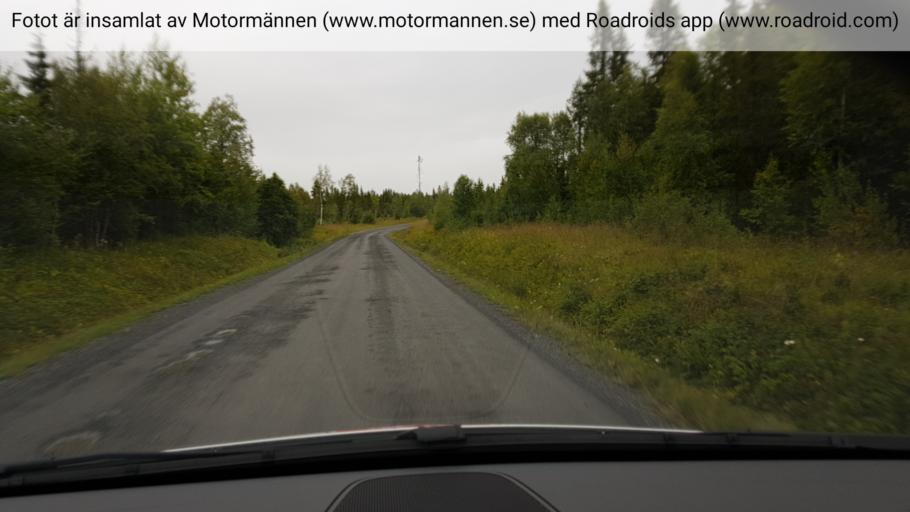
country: SE
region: Jaemtland
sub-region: OEstersunds Kommun
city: Lit
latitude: 63.5819
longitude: 14.9821
